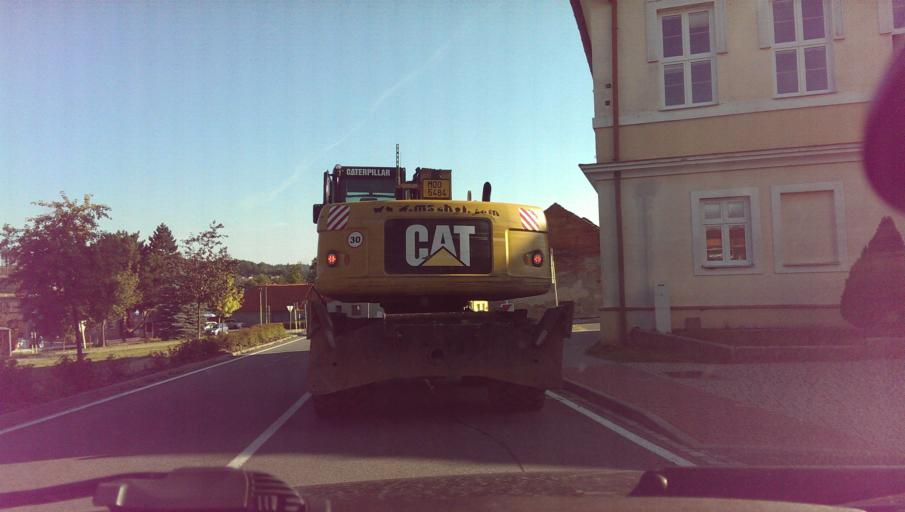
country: CZ
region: Olomoucky
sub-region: Okres Prerov
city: Hranice
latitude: 49.4990
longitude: 17.7391
